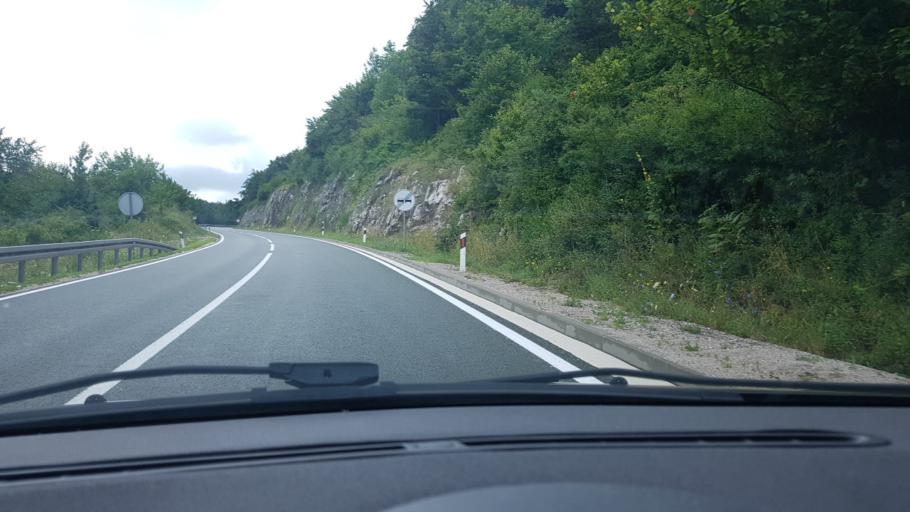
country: BA
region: Federation of Bosnia and Herzegovina
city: Izacic
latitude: 44.8656
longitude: 15.7013
